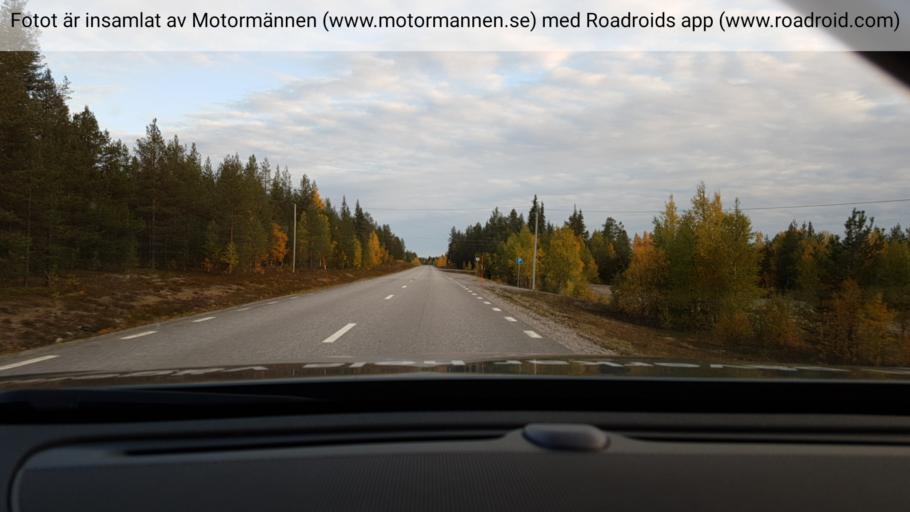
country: SE
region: Norrbotten
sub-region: Jokkmokks Kommun
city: Jokkmokk
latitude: 66.3903
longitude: 19.7043
